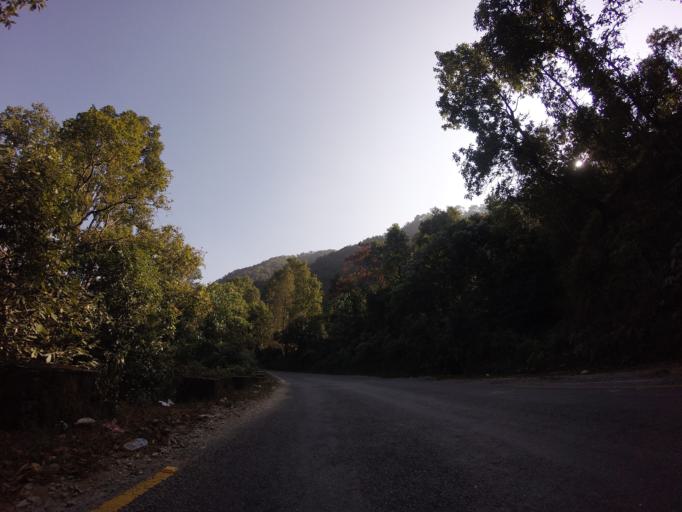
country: NP
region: Western Region
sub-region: Gandaki Zone
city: Pokhara
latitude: 28.1885
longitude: 83.9006
